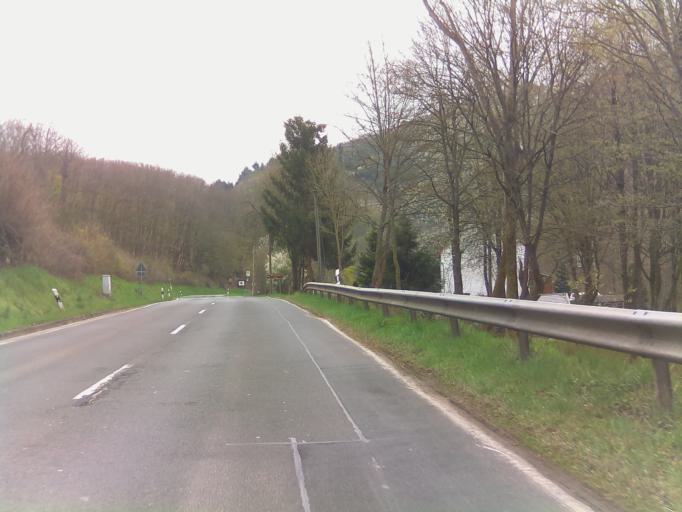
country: DE
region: Rheinland-Pfalz
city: Hennweiler
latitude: 49.8016
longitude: 7.4283
